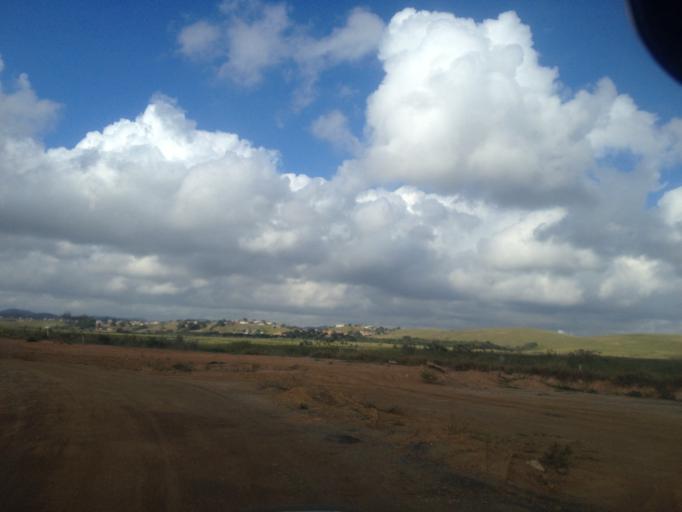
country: BR
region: Rio de Janeiro
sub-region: Resende
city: Resende
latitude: -22.4360
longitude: -44.3858
